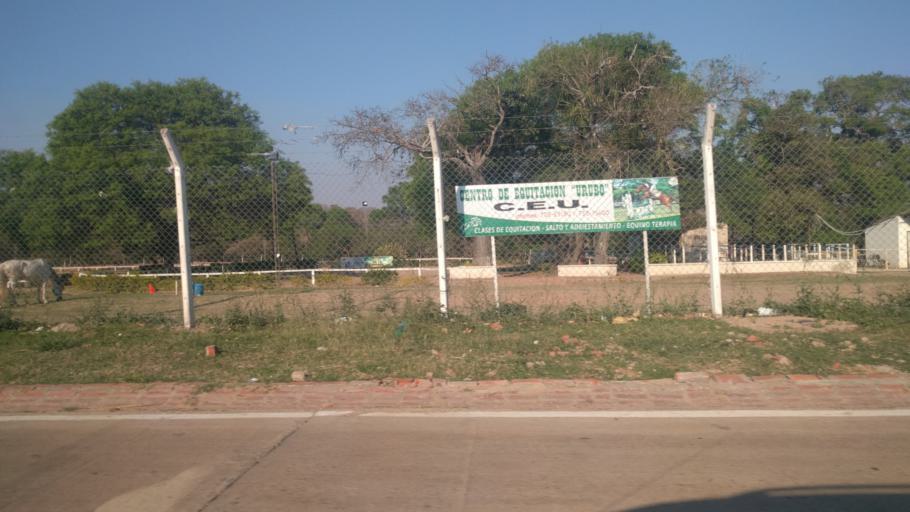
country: BO
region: Santa Cruz
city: Santa Cruz de la Sierra
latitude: -17.7529
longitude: -63.2161
